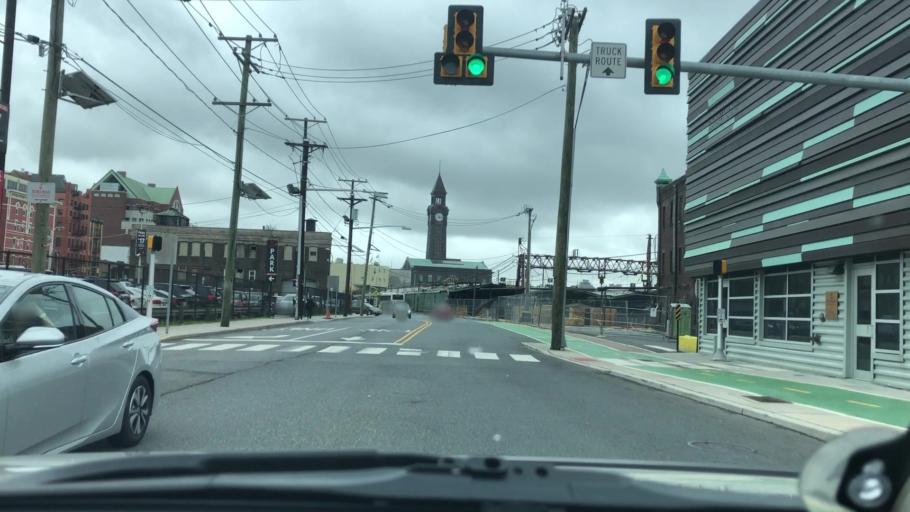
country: US
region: New Jersey
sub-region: Hudson County
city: Hoboken
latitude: 40.7356
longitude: -74.0315
